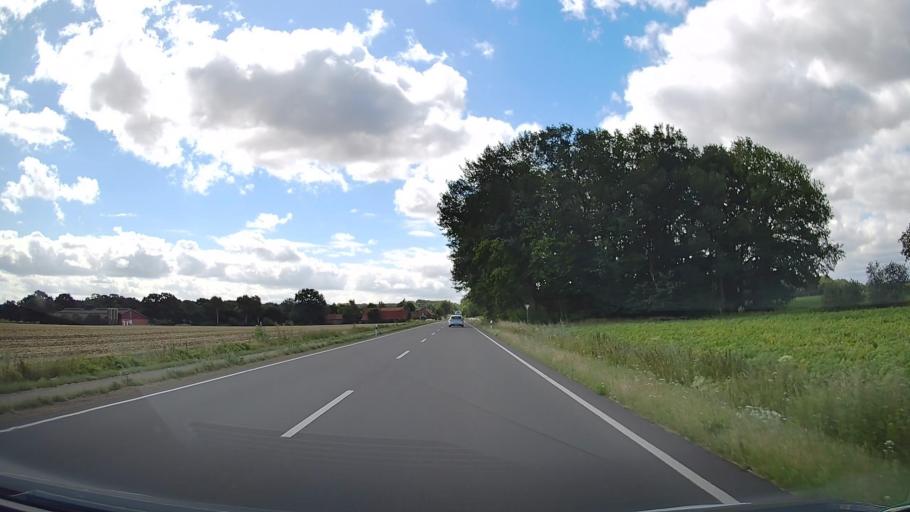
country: DE
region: Lower Saxony
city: Diepholz
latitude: 52.6670
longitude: 8.3285
